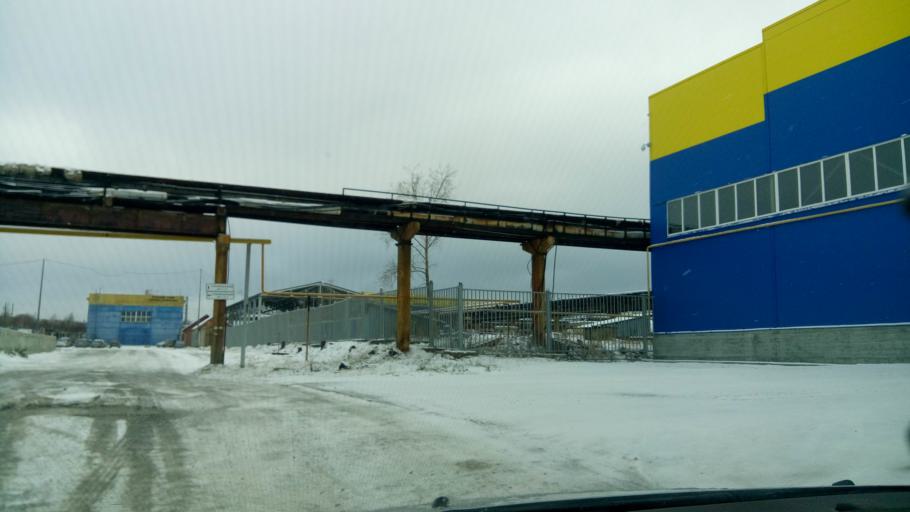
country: RU
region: Sverdlovsk
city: Polevskoy
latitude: 56.4706
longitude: 60.1758
